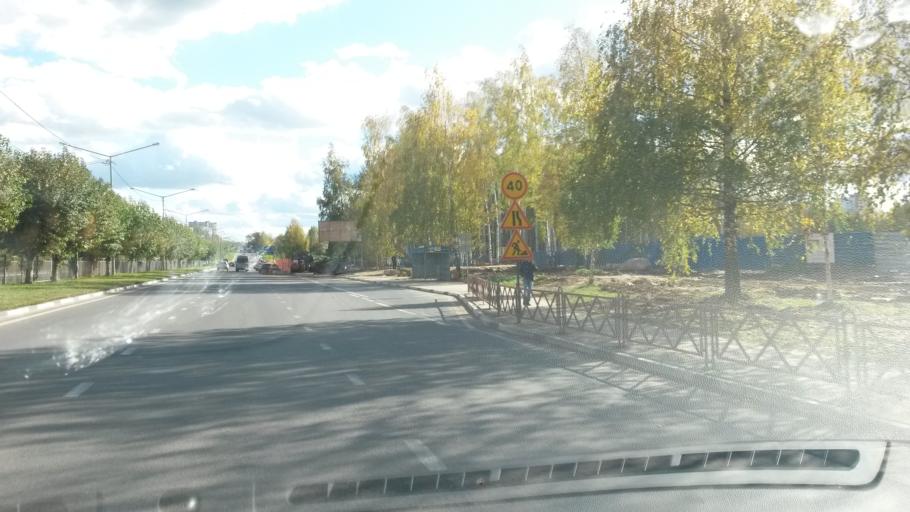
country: RU
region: Jaroslavl
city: Yaroslavl
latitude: 57.5772
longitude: 39.9157
